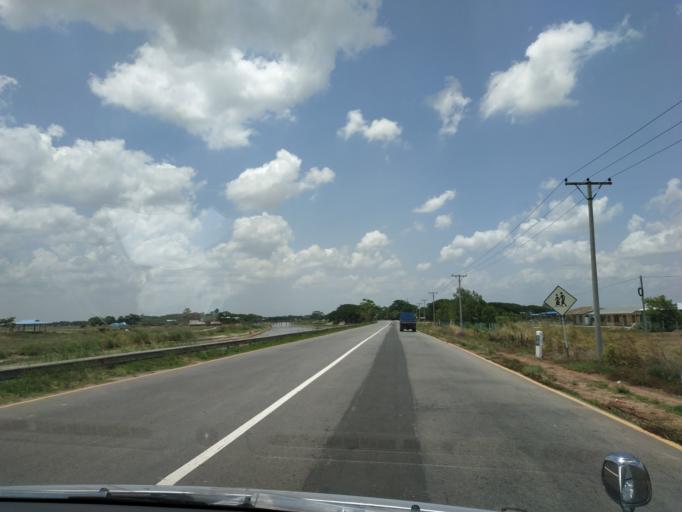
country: MM
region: Bago
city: Thanatpin
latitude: 17.5029
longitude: 96.7076
